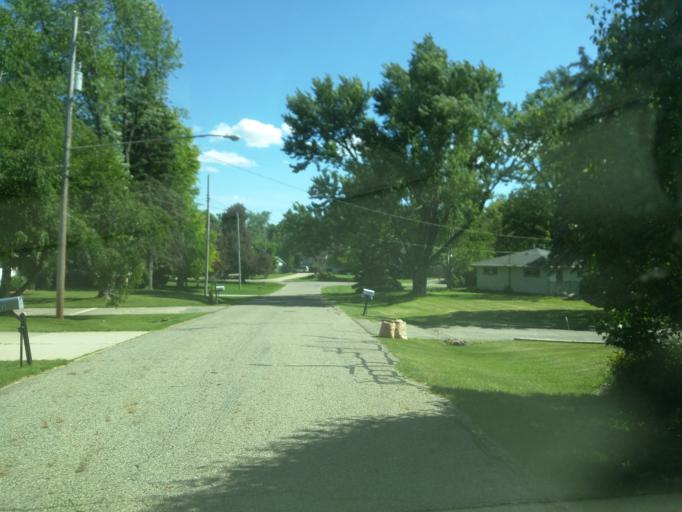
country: US
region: Michigan
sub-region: Ingham County
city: Edgemont Park
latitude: 42.7555
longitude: -84.5948
